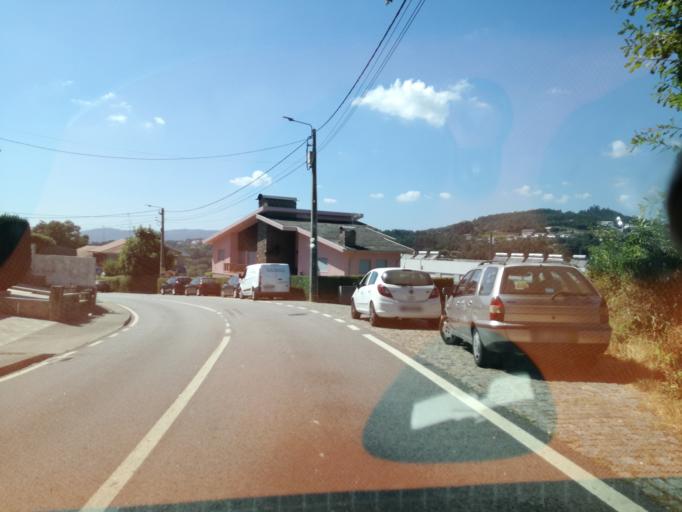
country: PT
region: Braga
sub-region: Guimaraes
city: Guimaraes
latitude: 41.4602
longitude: -8.2849
